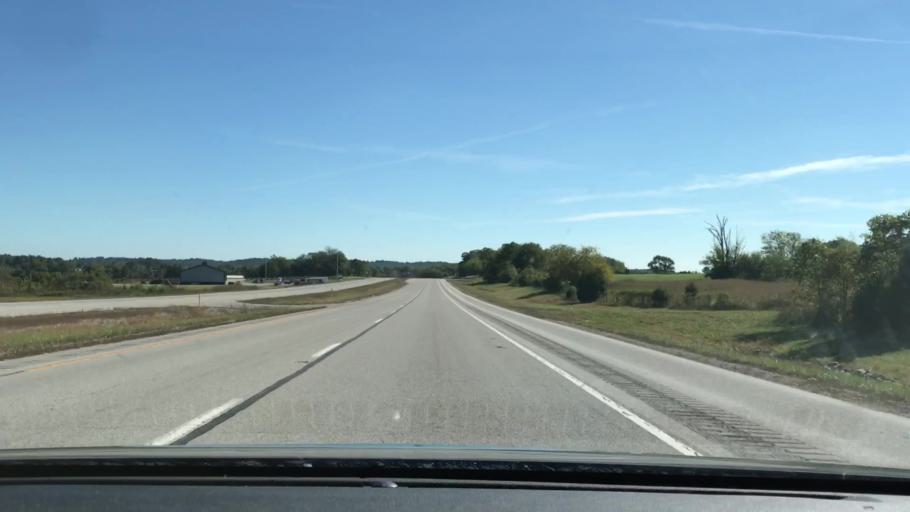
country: US
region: Kentucky
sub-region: Todd County
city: Elkton
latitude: 36.8210
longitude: -87.1804
